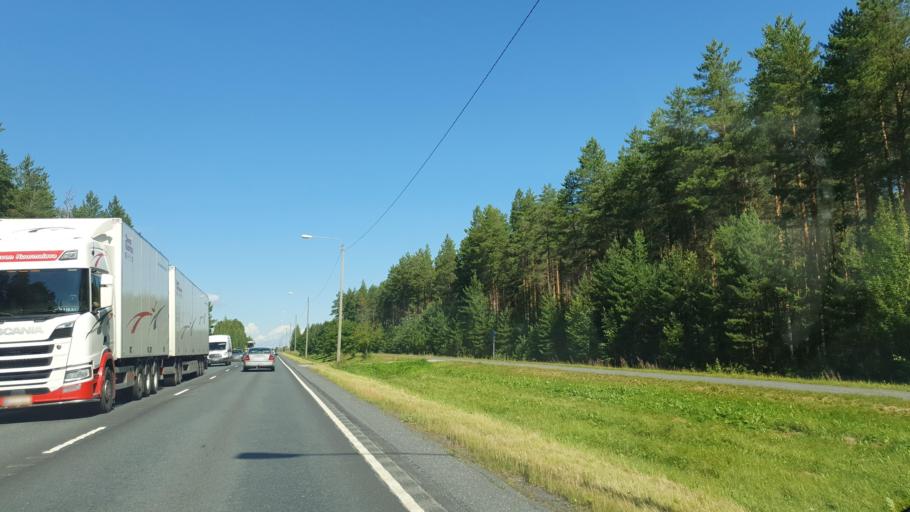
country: FI
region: Northern Savo
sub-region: Ylae-Savo
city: Lapinlahti
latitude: 63.4422
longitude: 27.3237
